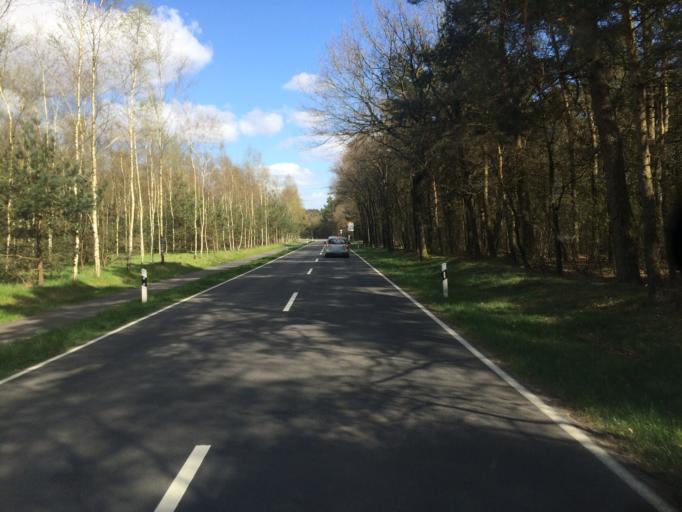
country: DE
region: Lower Saxony
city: Haren
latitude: 52.7711
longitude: 7.1974
